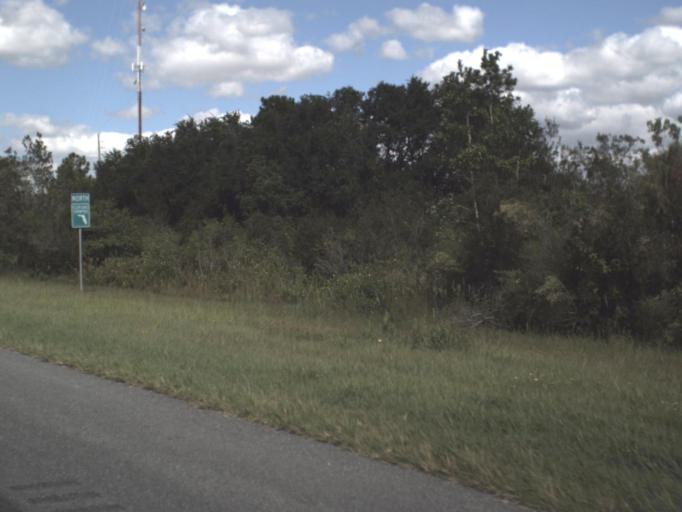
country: US
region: Florida
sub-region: Osceola County
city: Buenaventura Lakes
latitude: 28.2916
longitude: -81.3503
